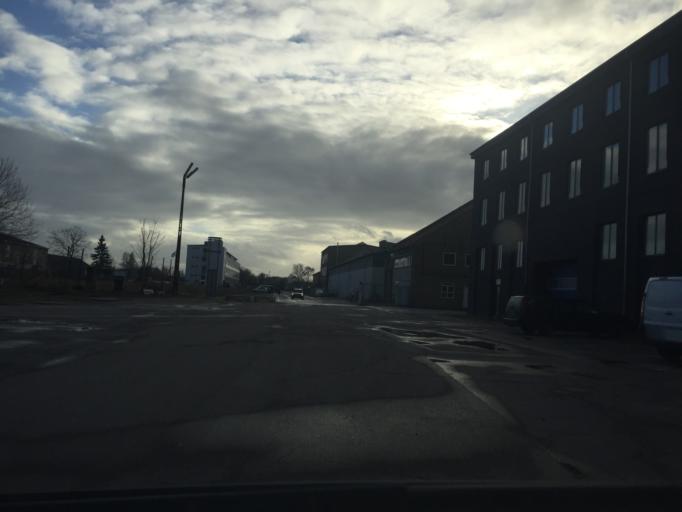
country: DK
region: Capital Region
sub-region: Kobenhavn
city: Christianshavn
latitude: 55.6920
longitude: 12.6125
